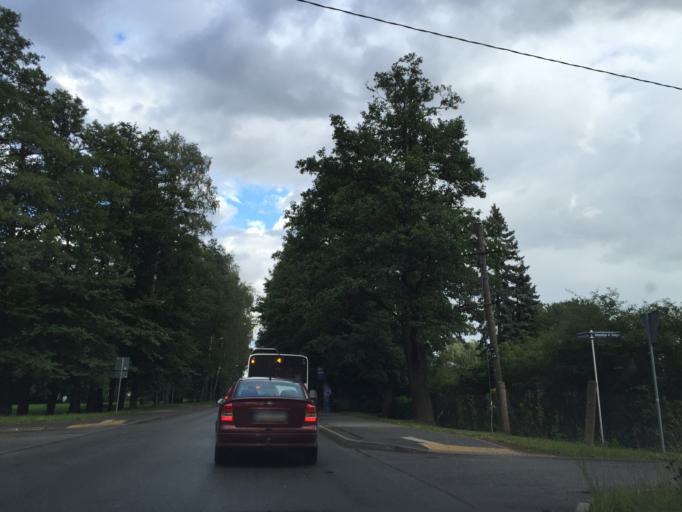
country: LV
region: Marupe
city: Marupe
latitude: 56.9521
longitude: 24.0296
